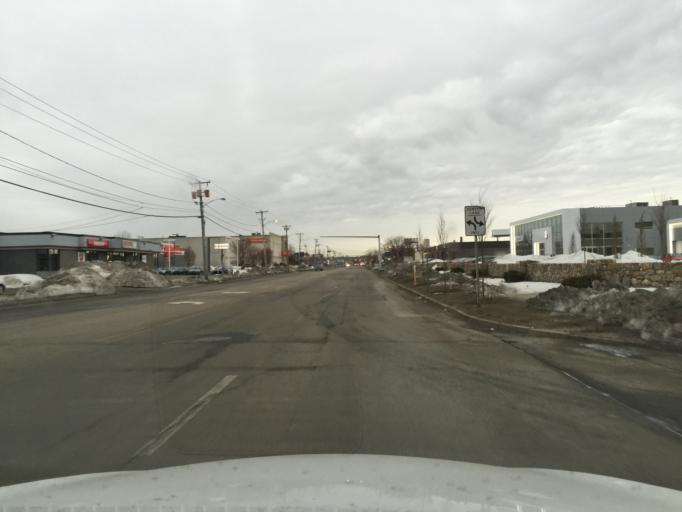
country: US
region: Massachusetts
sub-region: Middlesex County
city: Somerville
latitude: 42.4024
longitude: -71.0984
